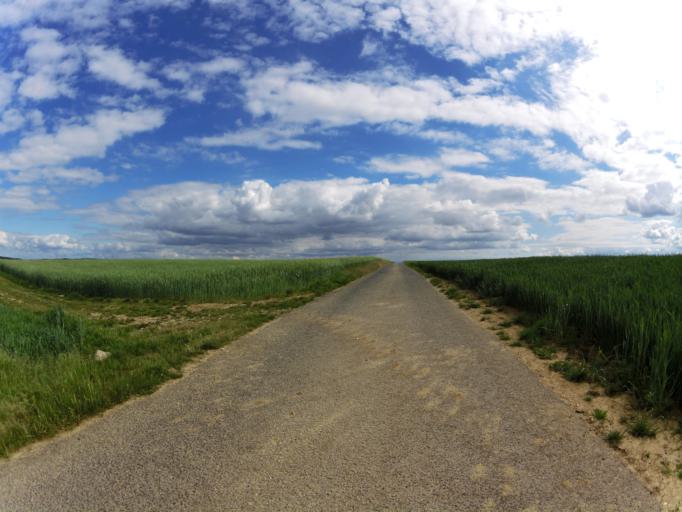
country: DE
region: Bavaria
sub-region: Regierungsbezirk Unterfranken
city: Gaukonigshofen
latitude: 49.6529
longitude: 10.0103
